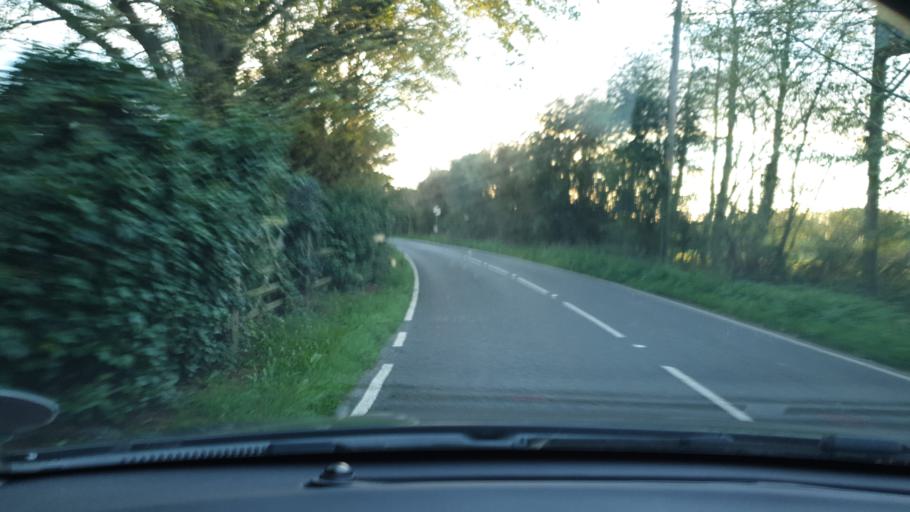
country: GB
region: England
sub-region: Essex
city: Alresford
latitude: 51.9062
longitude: 1.0011
